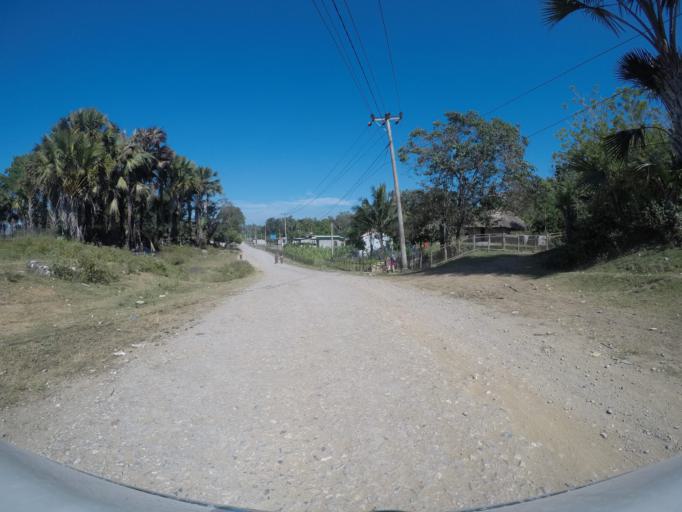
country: TL
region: Viqueque
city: Viqueque
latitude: -8.9752
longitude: 126.0496
